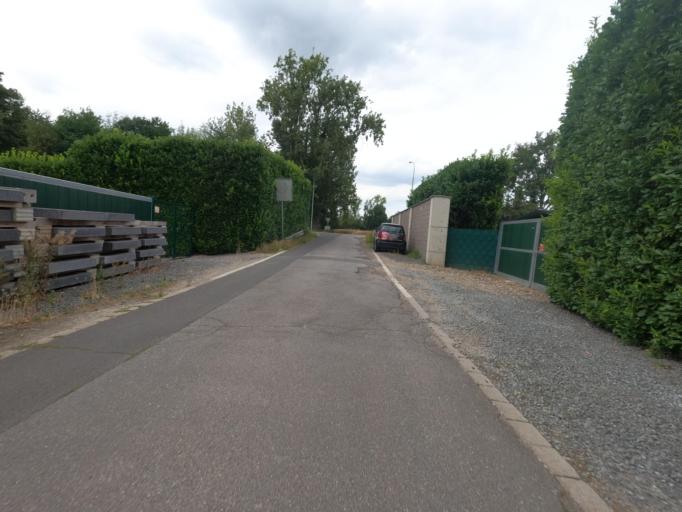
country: DE
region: North Rhine-Westphalia
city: Siersdorf
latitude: 50.9019
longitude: 6.2267
